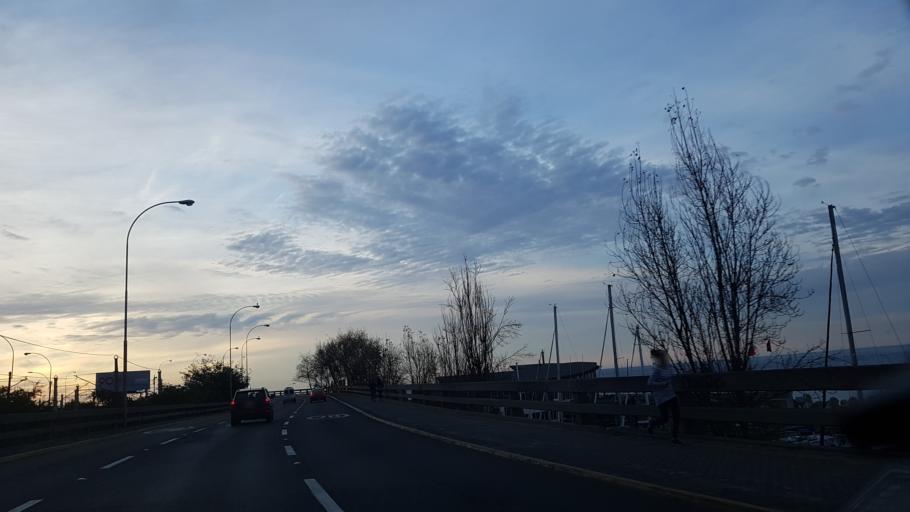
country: CL
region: Valparaiso
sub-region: Provincia de Valparaiso
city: Vina del Mar
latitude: -33.0270
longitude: -71.5808
